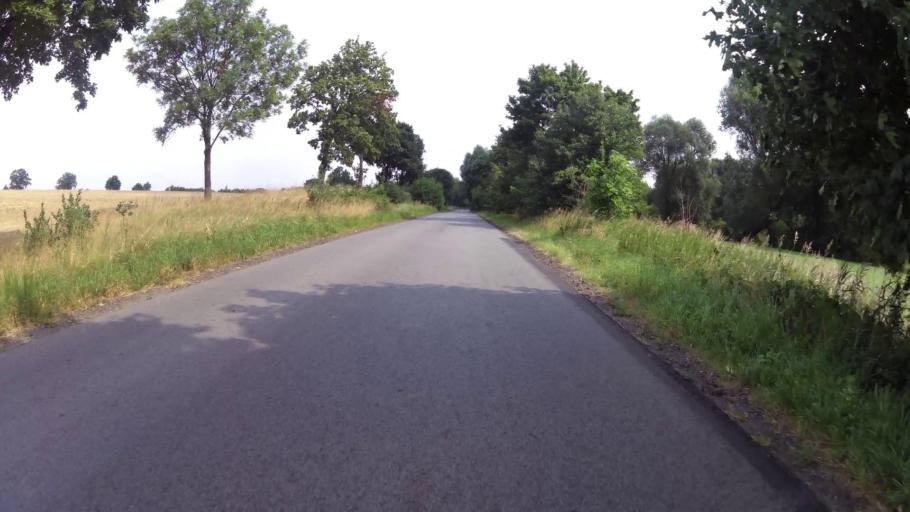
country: PL
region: West Pomeranian Voivodeship
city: Trzcinsko Zdroj
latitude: 52.9263
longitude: 14.6483
